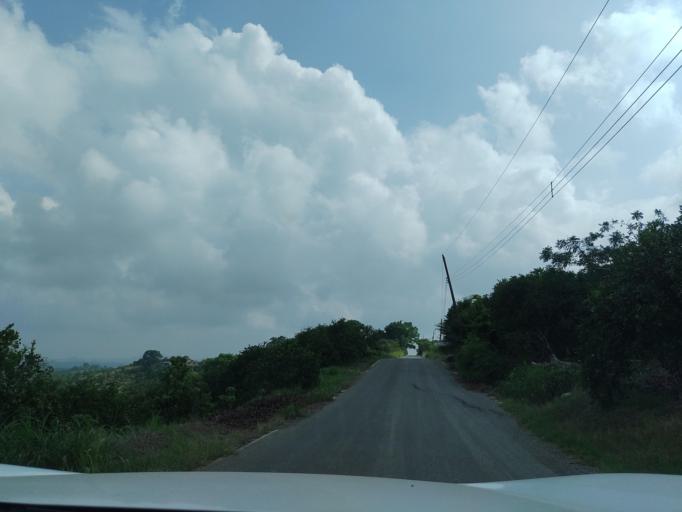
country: MX
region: Veracruz
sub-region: Martinez de la Torre
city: La Union Paso Largo
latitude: 20.2275
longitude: -97.0844
